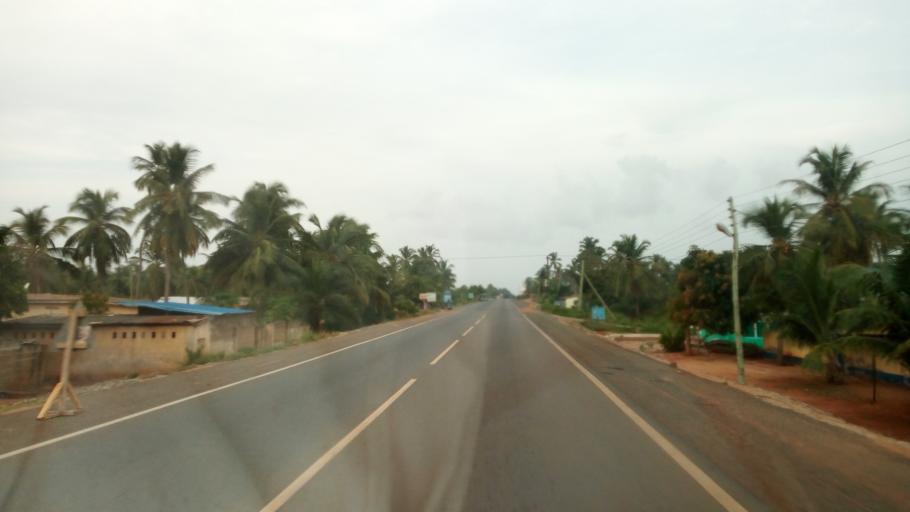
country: TG
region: Maritime
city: Lome
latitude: 6.0869
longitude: 1.0626
